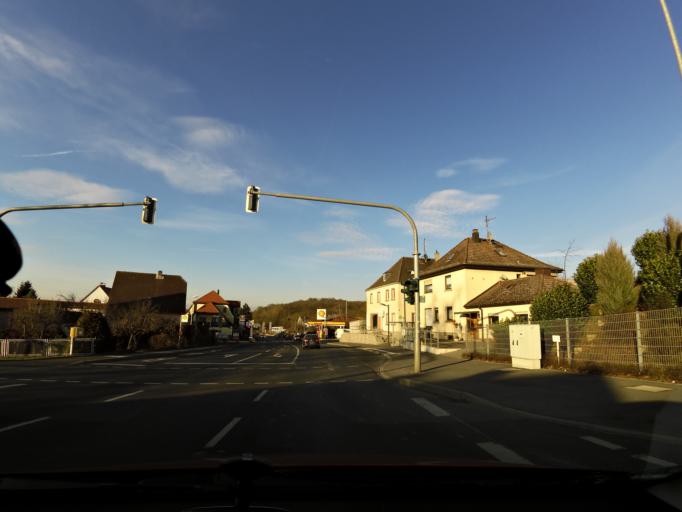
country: DE
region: Bavaria
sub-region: Regierungsbezirk Unterfranken
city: Kist
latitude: 49.7443
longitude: 9.8450
